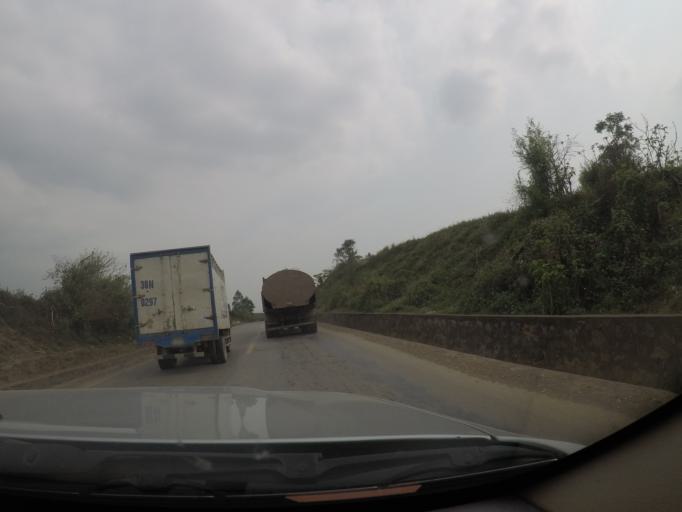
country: VN
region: Thanh Hoa
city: Thi Tran Ben Sung
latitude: 19.3852
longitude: 105.4596
